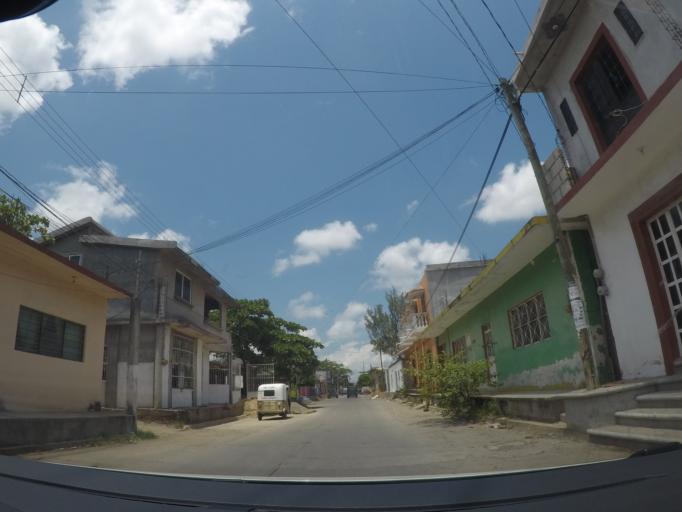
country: MX
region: Oaxaca
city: Juchitan de Zaragoza
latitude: 16.4408
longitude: -95.0198
